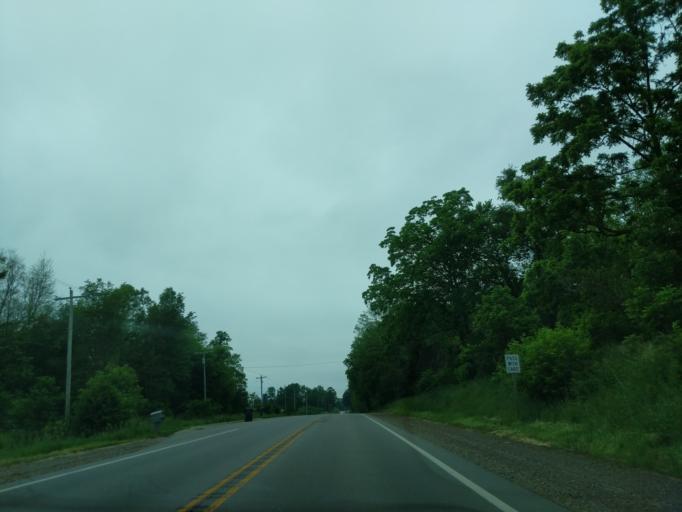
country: US
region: Michigan
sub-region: Branch County
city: Quincy
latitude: 41.9510
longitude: -84.7998
